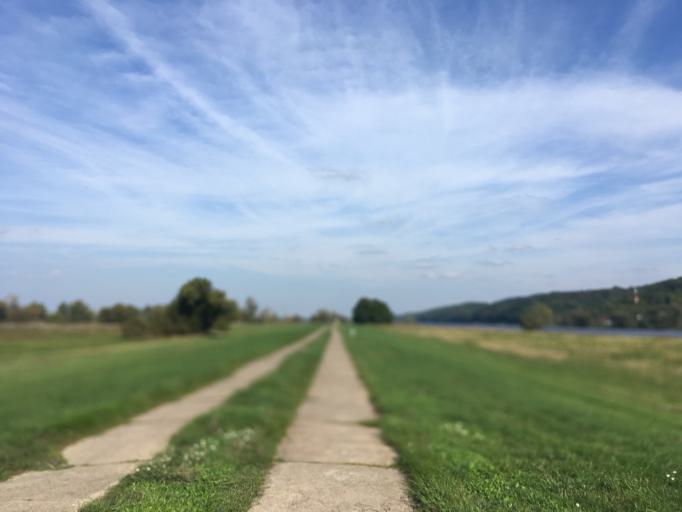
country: DE
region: Brandenburg
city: Meyenburg
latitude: 53.0108
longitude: 14.2678
